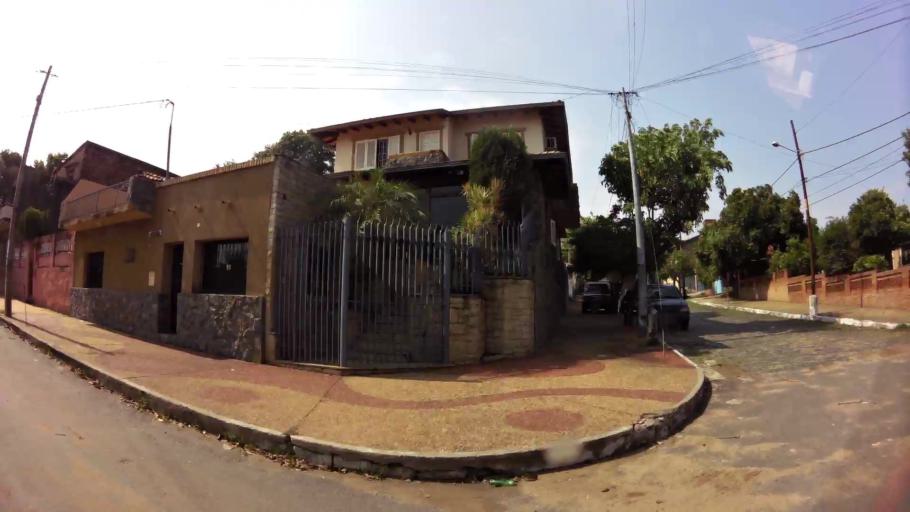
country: PY
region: Presidente Hayes
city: Nanawa
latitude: -25.2815
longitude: -57.6577
